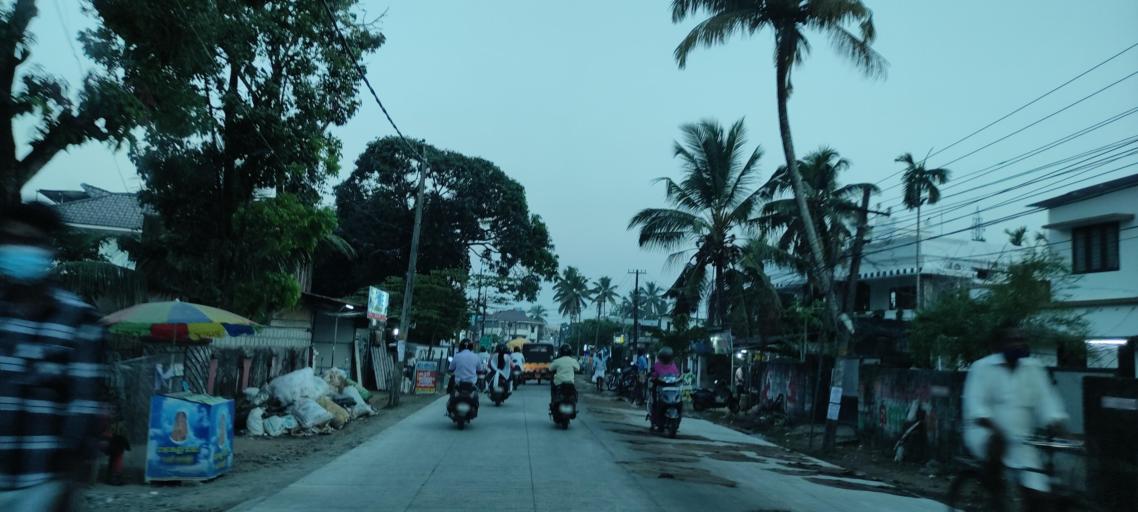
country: IN
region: Kerala
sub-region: Alappuzha
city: Alleppey
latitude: 9.5154
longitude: 76.3364
